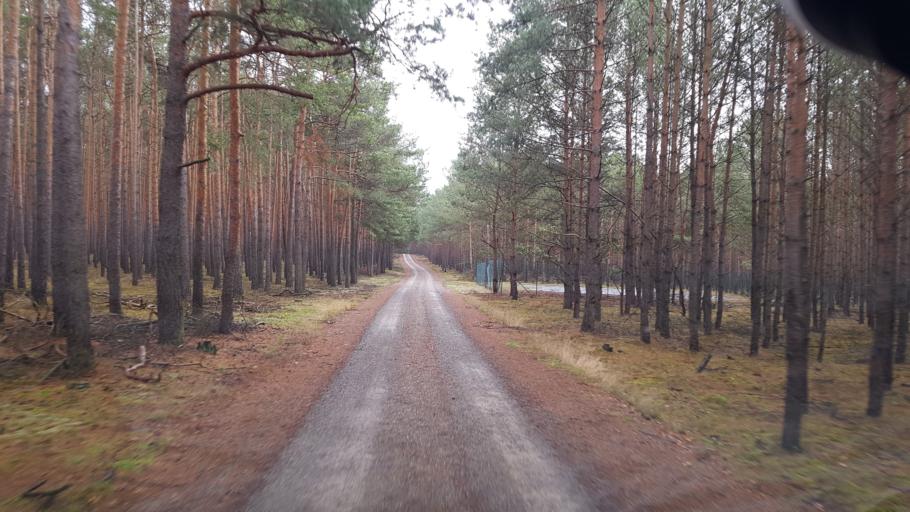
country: DE
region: Brandenburg
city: Hohenbucko
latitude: 51.7482
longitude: 13.4310
